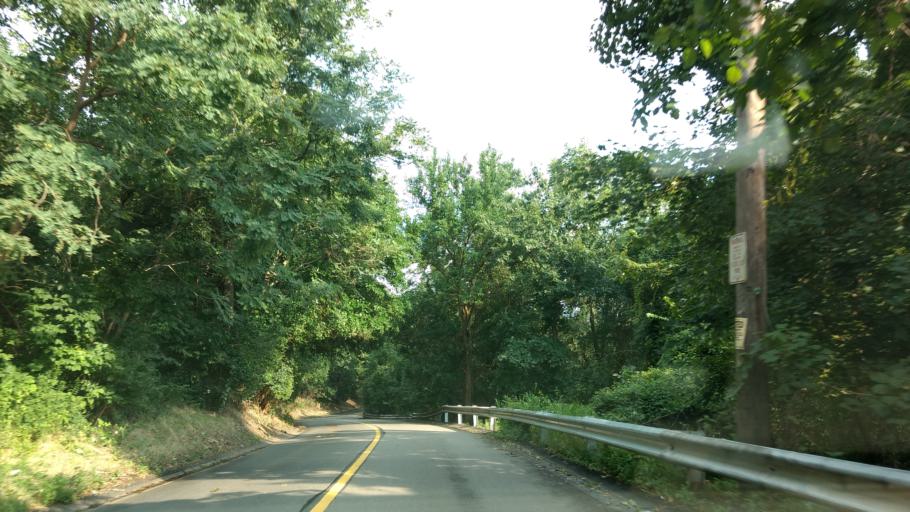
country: US
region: Pennsylvania
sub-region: Allegheny County
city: Bellevue
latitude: 40.4927
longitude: -80.0368
